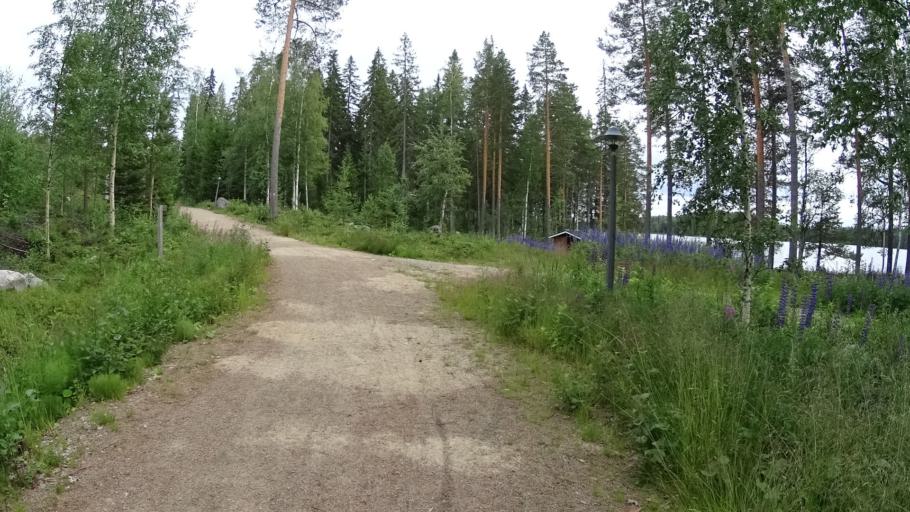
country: FI
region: Southern Ostrobothnia
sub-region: Kuusiokunnat
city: AEhtaeri
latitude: 62.5313
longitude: 24.1875
